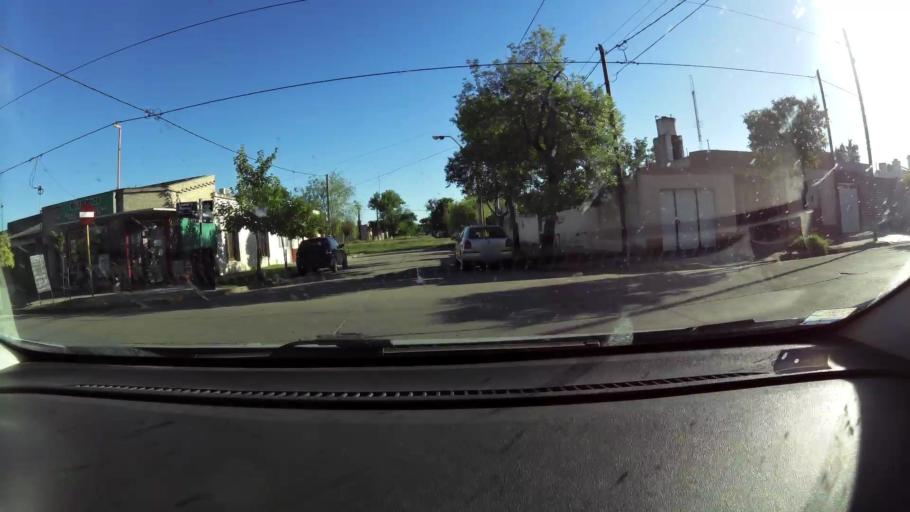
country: AR
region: Cordoba
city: San Francisco
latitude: -31.4376
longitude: -62.0912
